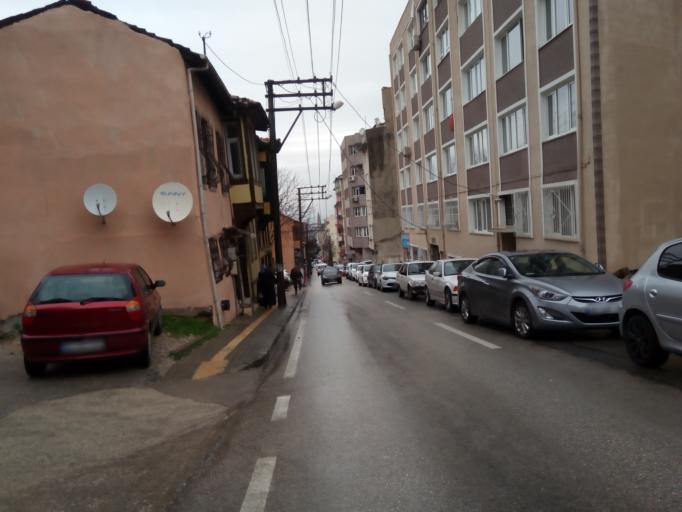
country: TR
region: Bursa
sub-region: Osmangazi
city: Bursa
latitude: 40.1790
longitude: 29.0620
